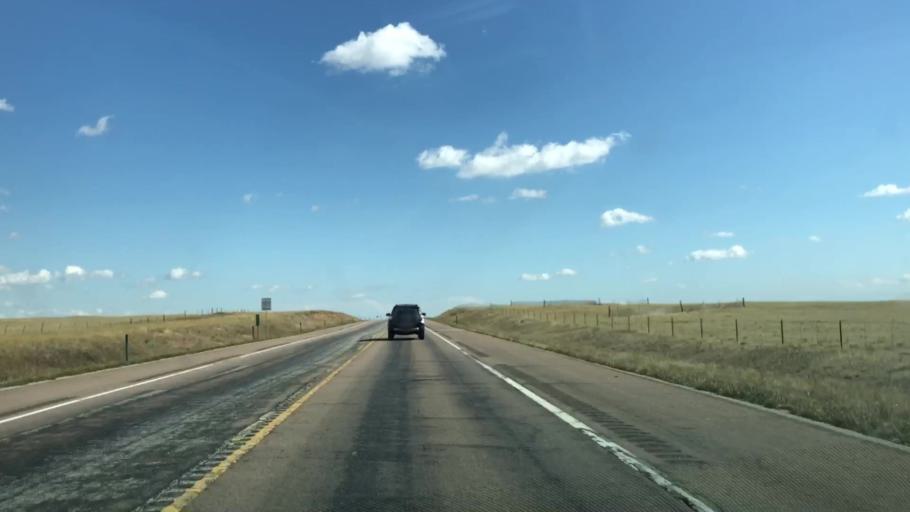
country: US
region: Colorado
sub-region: Larimer County
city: Laporte
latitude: 40.9130
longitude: -105.3173
